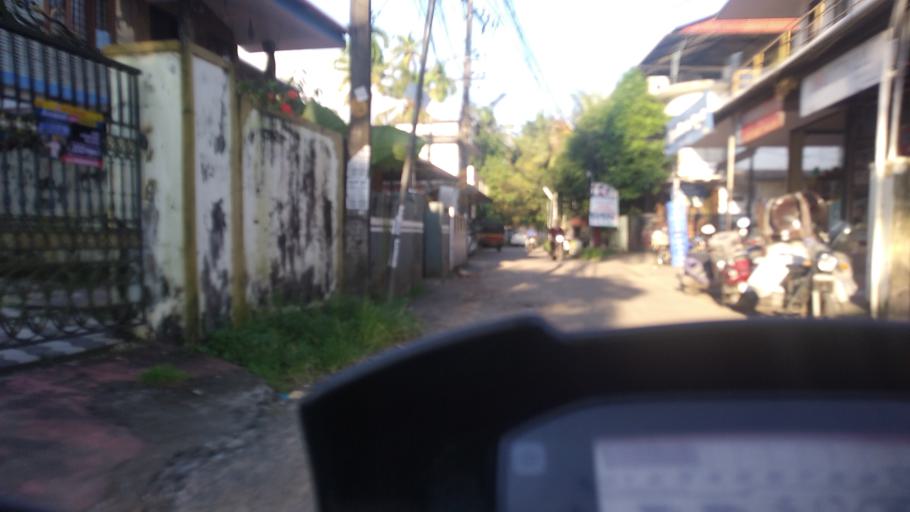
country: IN
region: Kerala
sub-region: Ernakulam
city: Cochin
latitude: 9.9452
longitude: 76.3269
